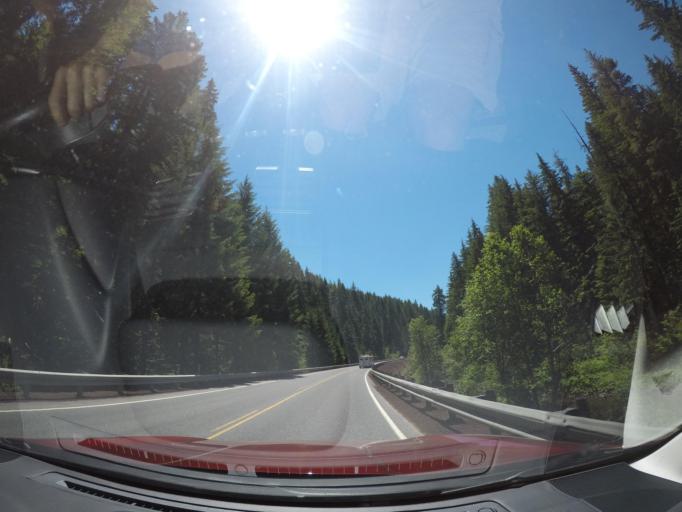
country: US
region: Oregon
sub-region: Deschutes County
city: Sisters
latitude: 44.5537
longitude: -121.9940
